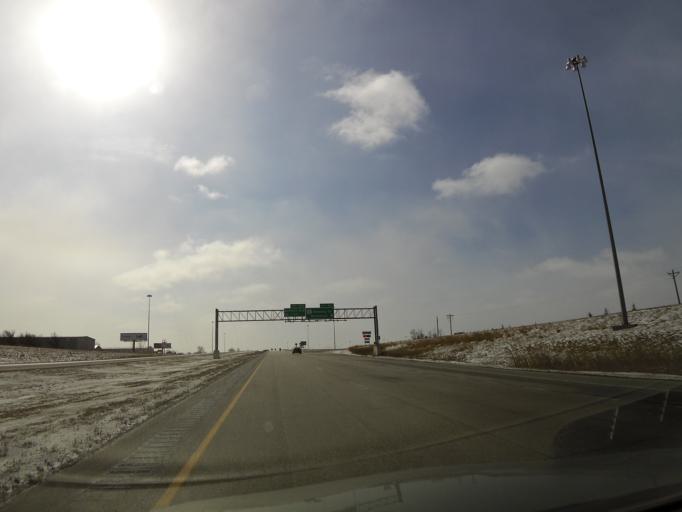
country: US
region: North Dakota
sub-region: Grand Forks County
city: Grand Forks
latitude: 47.9391
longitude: -97.0937
